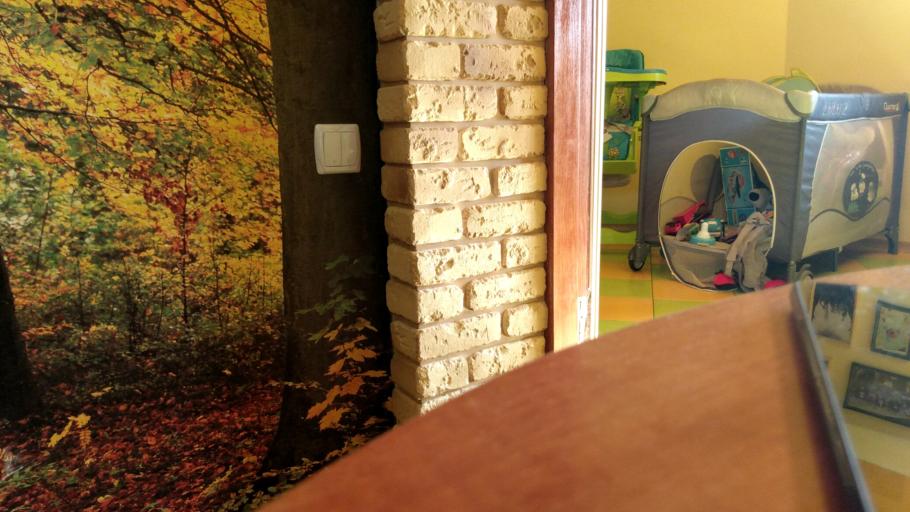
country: RU
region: Tverskaya
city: Gorodnya
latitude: 56.7484
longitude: 36.3332
